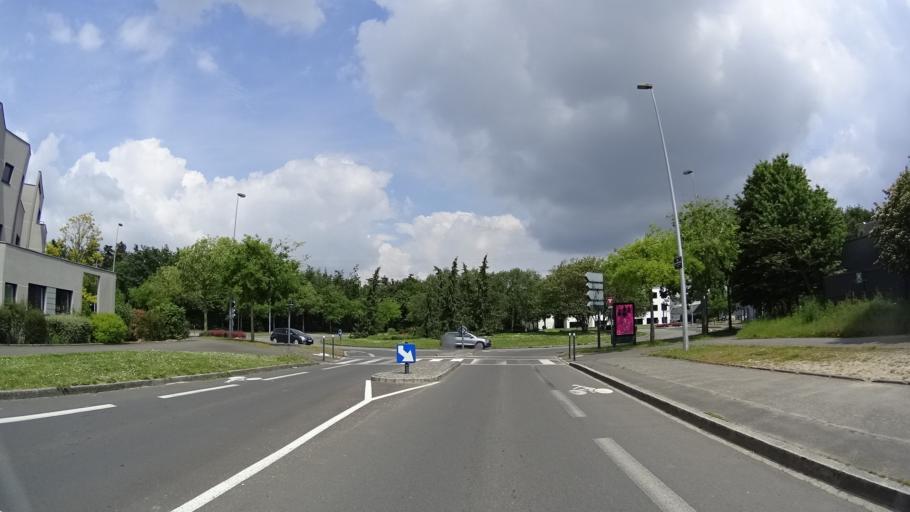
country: FR
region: Brittany
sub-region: Departement d'Ille-et-Vilaine
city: Rennes
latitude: 48.1046
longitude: -1.7082
